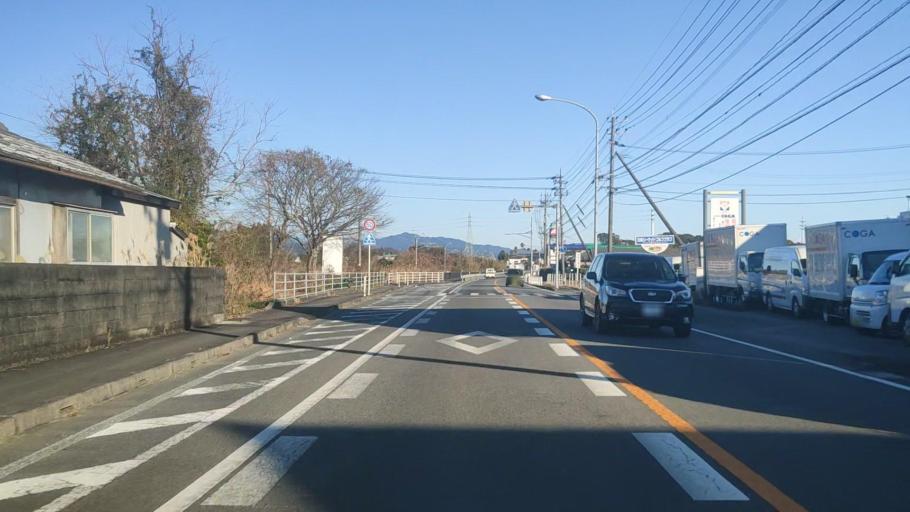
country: JP
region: Miyazaki
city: Nobeoka
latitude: 32.3876
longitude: 131.6275
